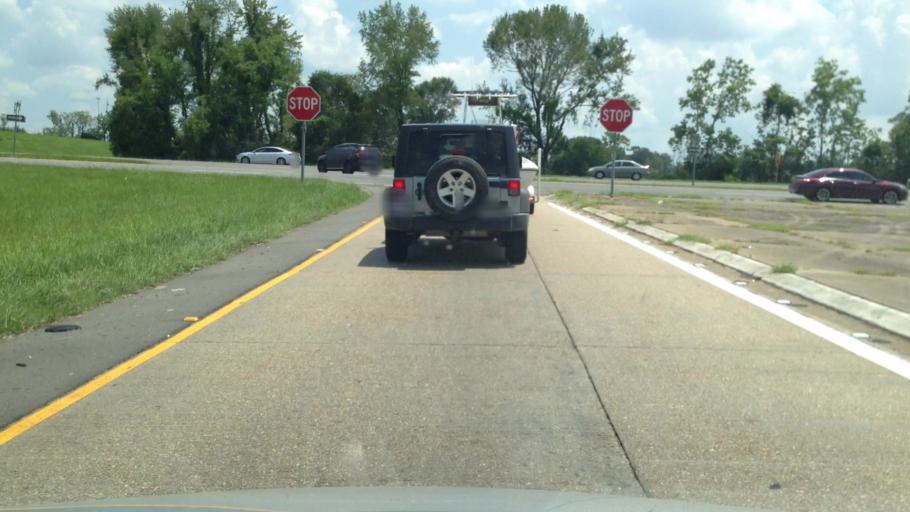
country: US
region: Louisiana
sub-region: Saint Landry Parish
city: Opelousas
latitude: 30.5319
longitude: -92.0674
